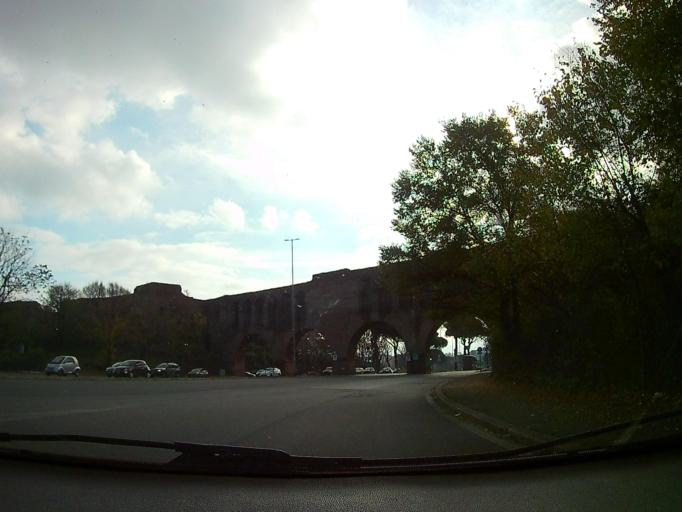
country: IT
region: Latium
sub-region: Citta metropolitana di Roma Capitale
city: Rome
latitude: 41.8742
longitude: 12.4963
